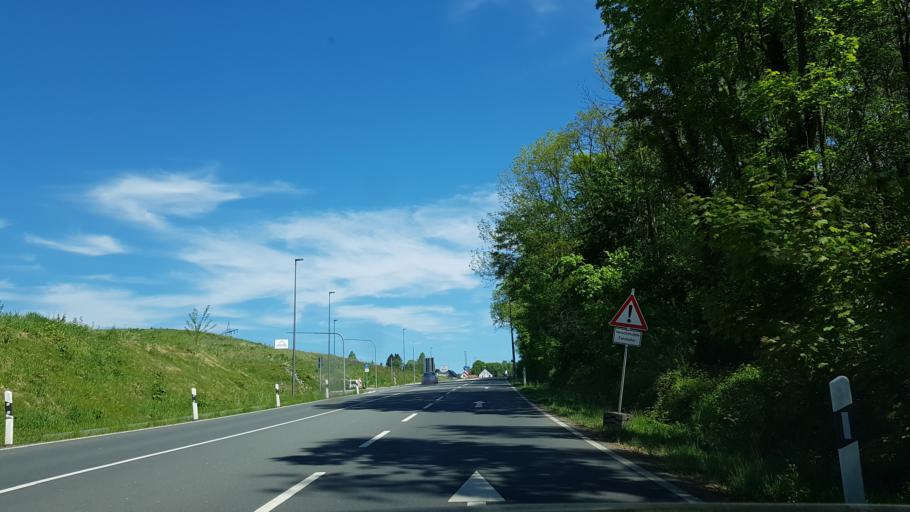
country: DE
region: North Rhine-Westphalia
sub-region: Regierungsbezirk Dusseldorf
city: Heiligenhaus
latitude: 51.3102
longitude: 6.9511
